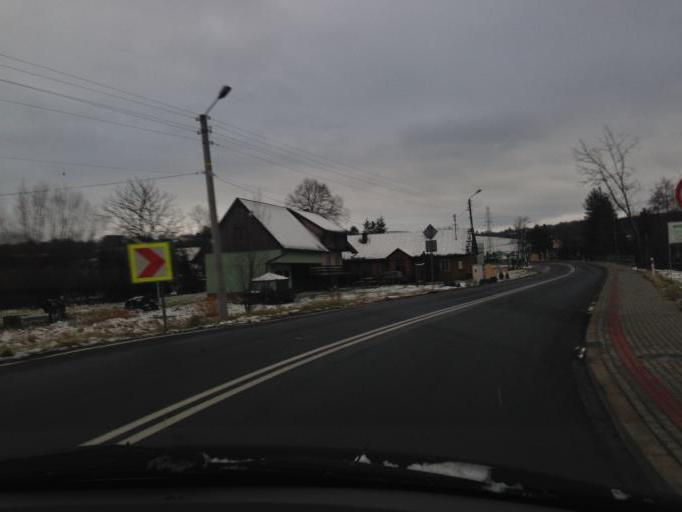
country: PL
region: Lesser Poland Voivodeship
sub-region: Powiat tarnowski
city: Gromnik
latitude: 49.8388
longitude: 20.9846
